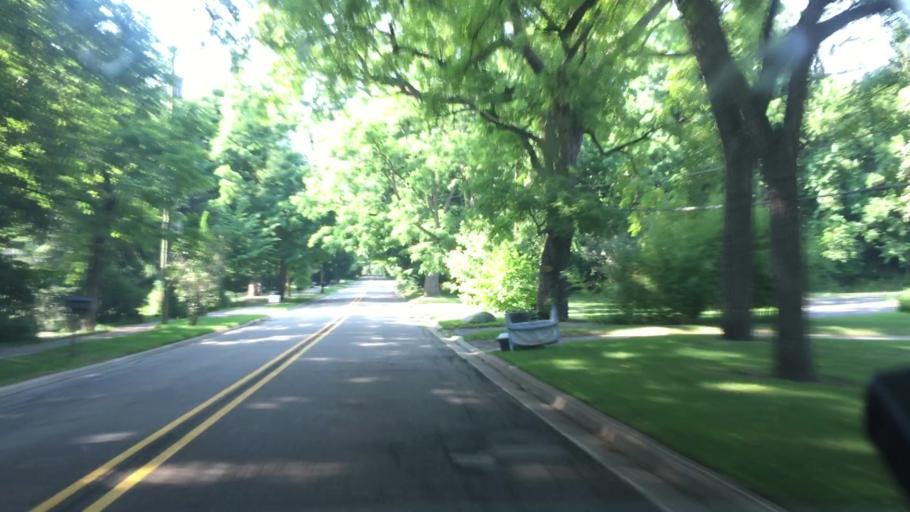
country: US
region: Michigan
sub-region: Oakland County
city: Franklin
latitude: 42.5349
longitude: -83.2952
